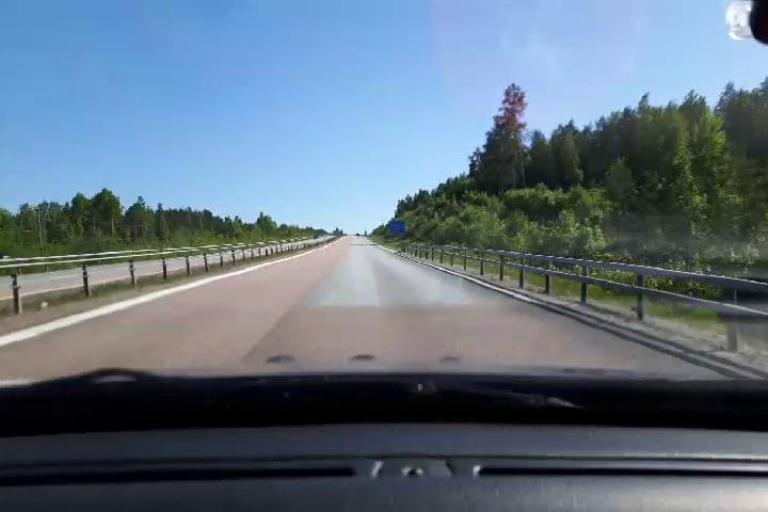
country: SE
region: Gaevleborg
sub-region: Soderhamns Kommun
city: Soderhamn
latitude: 61.3519
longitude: 17.0172
